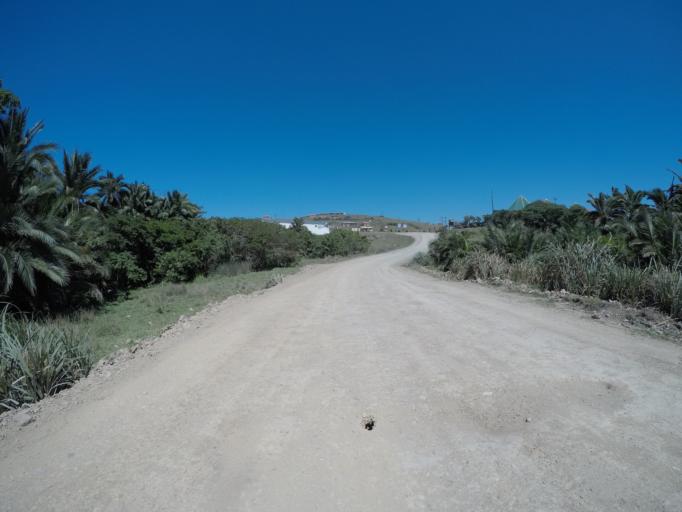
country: ZA
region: Eastern Cape
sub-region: OR Tambo District Municipality
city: Libode
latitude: -32.0313
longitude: 29.1100
